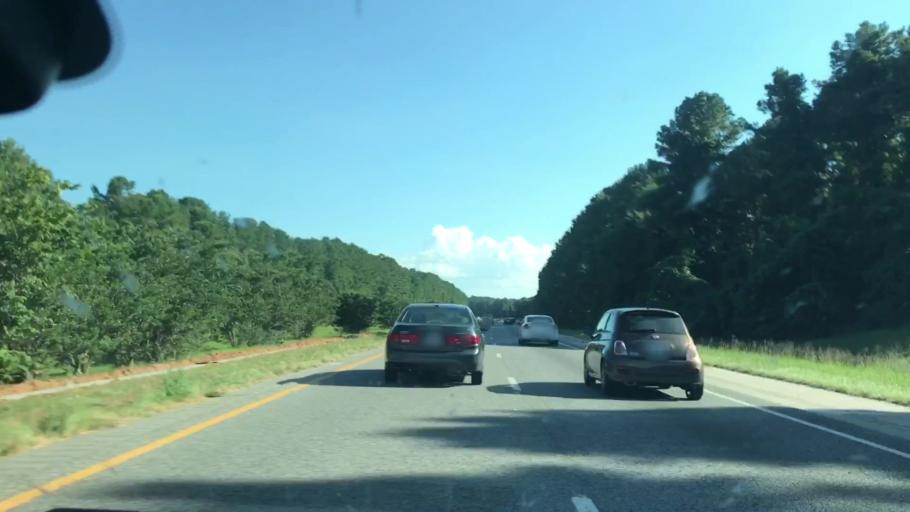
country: US
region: Georgia
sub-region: Harris County
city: Hamilton
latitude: 32.7826
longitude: -85.0203
